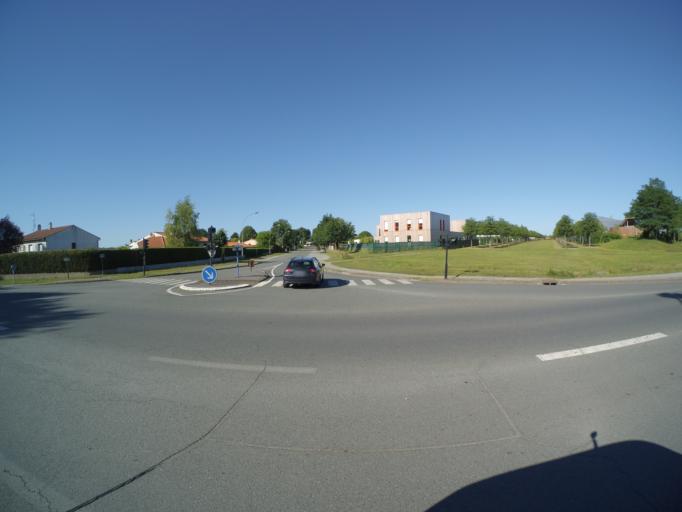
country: FR
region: Pays de la Loire
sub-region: Departement de la Vendee
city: Les Herbiers
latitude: 46.8620
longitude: -1.0220
